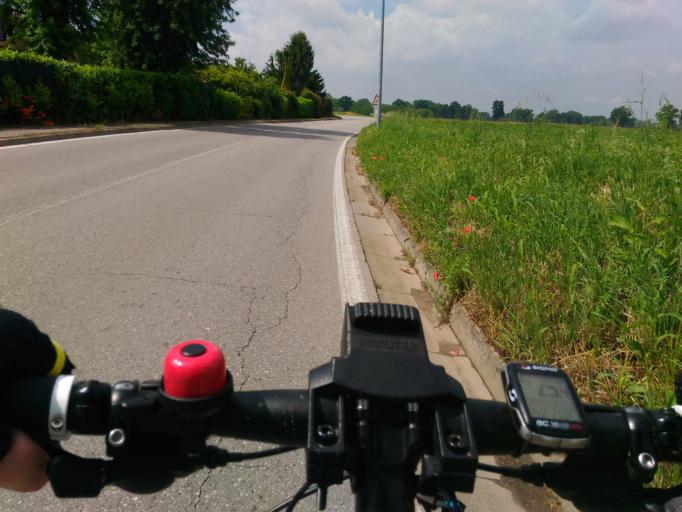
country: IT
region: Lombardy
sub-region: Provincia di Lodi
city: Mairago
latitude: 45.2637
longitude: 9.5876
